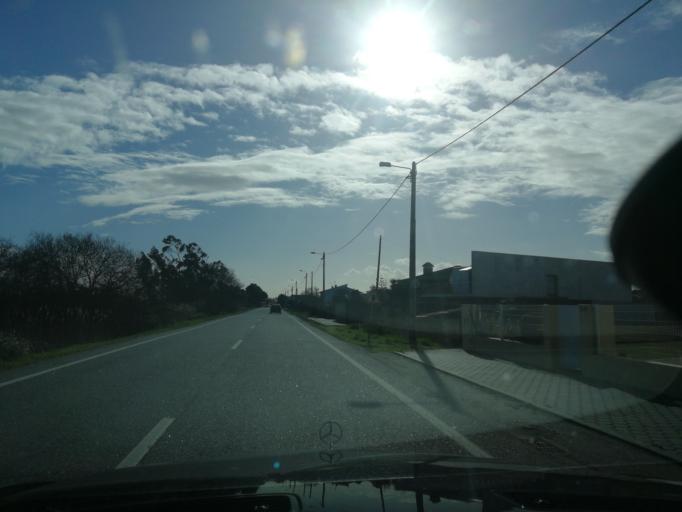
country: PT
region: Aveiro
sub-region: Estarreja
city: Pardilho
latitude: 40.8262
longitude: -8.6665
